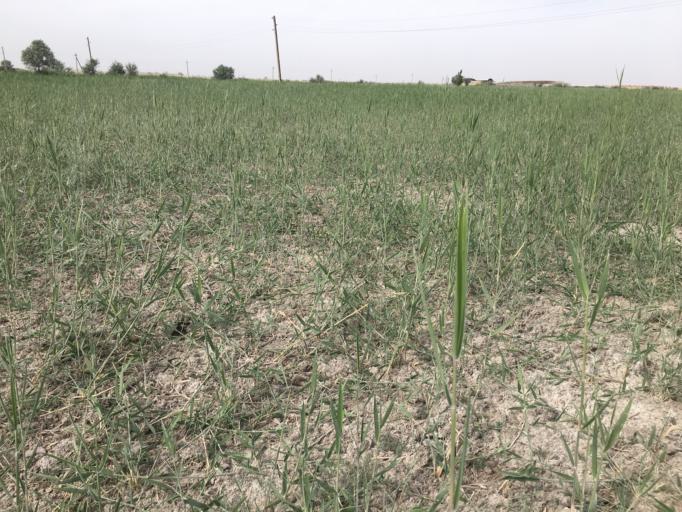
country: TM
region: Dasoguz
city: Tagta
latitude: 41.5594
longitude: 59.8124
